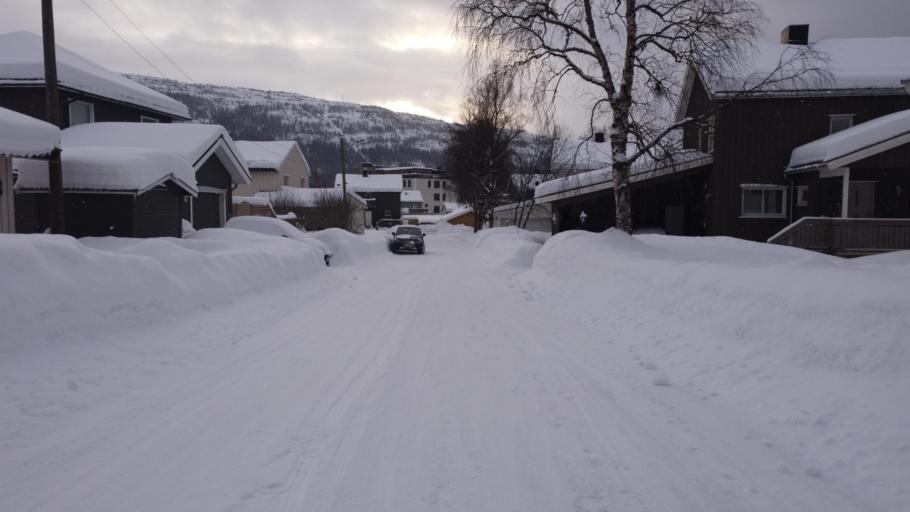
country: NO
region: Nordland
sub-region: Rana
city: Mo i Rana
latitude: 66.3139
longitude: 14.1481
